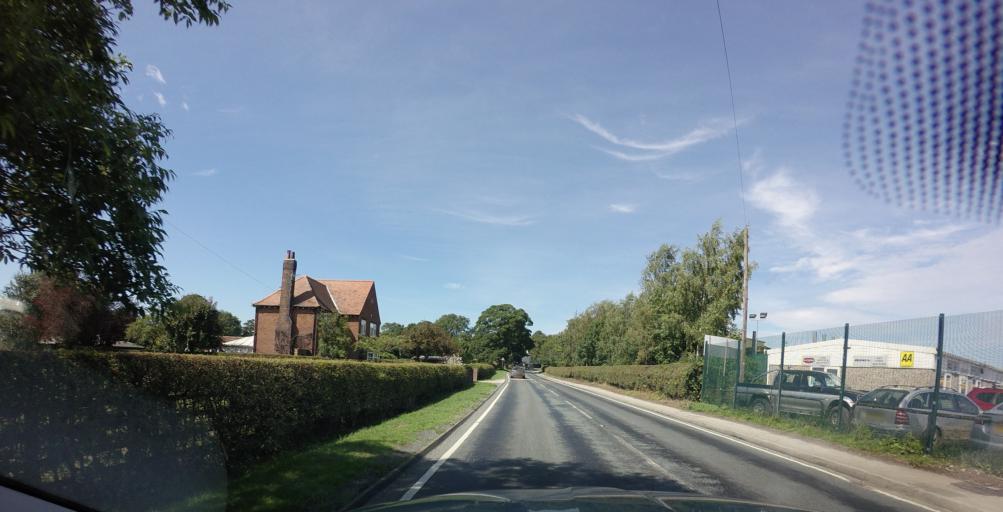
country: GB
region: England
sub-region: North Yorkshire
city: Ripon
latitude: 54.1285
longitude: -1.5035
